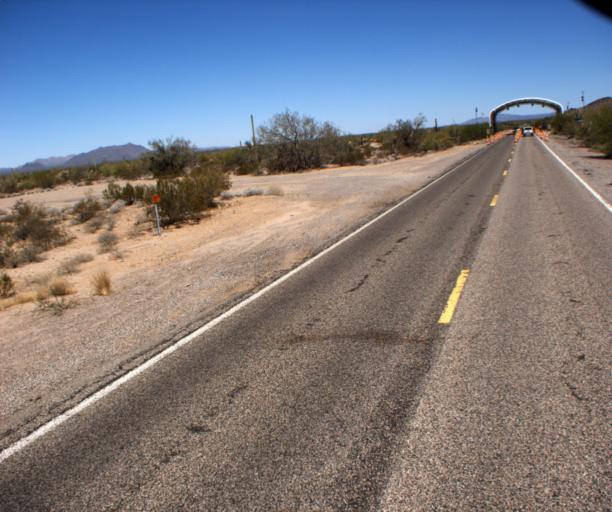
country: US
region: Arizona
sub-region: Pima County
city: Ajo
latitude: 32.2009
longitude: -112.7593
